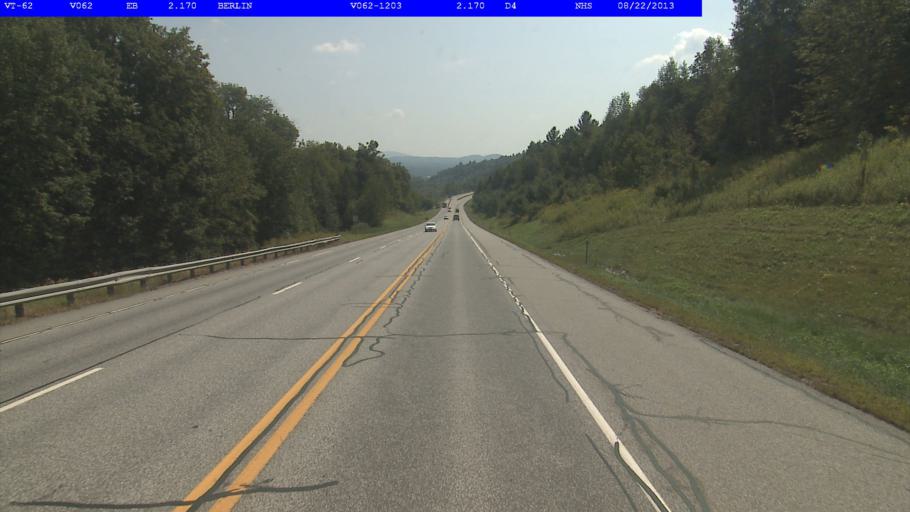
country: US
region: Vermont
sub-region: Washington County
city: Barre
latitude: 44.2183
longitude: -72.5471
